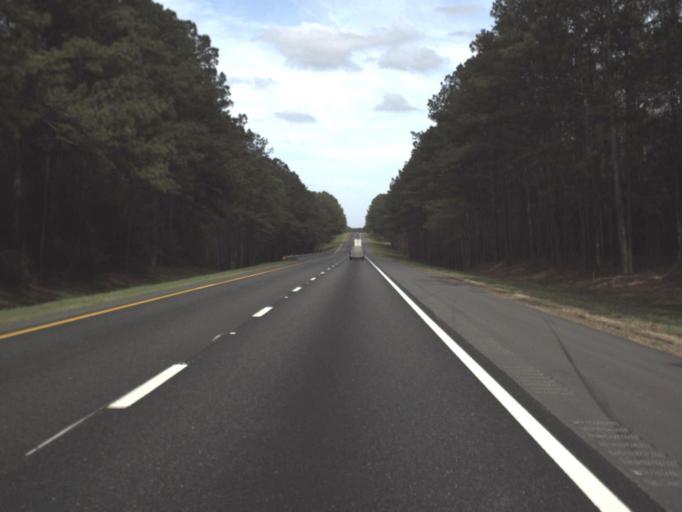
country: US
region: Florida
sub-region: Walton County
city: DeFuniak Springs
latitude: 30.6961
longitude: -85.9905
